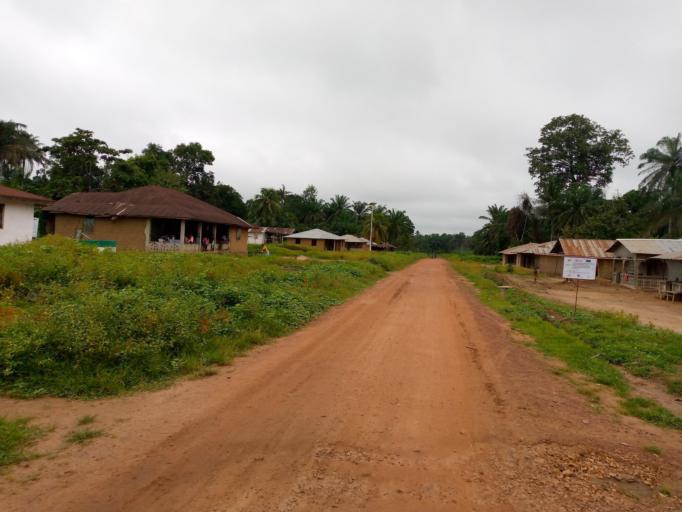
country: SL
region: Southern Province
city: Sumbuya
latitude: 7.5950
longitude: -12.0846
